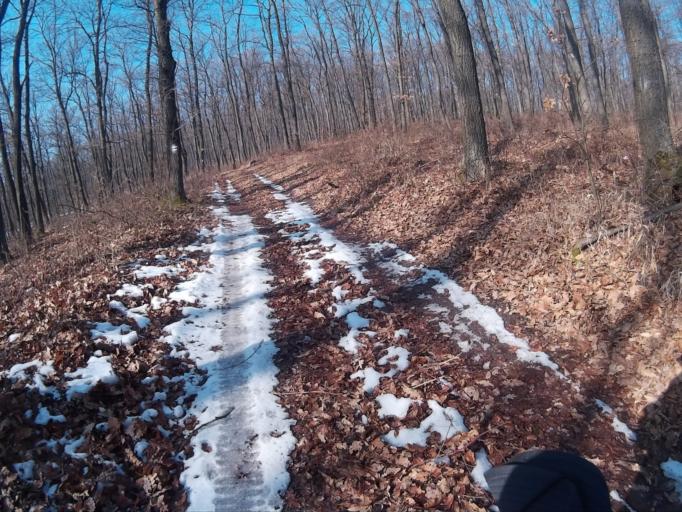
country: HU
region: Nograd
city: Paszto
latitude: 47.9830
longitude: 19.6742
